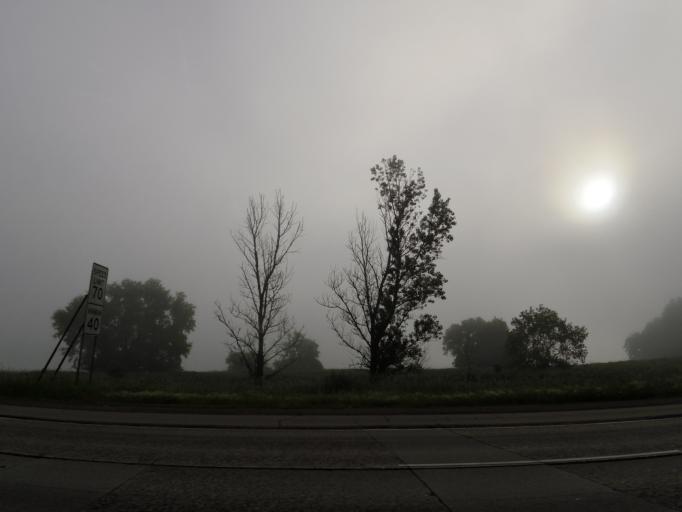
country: US
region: Minnesota
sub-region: Hennepin County
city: Maple Grove
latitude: 45.1145
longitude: -93.4754
